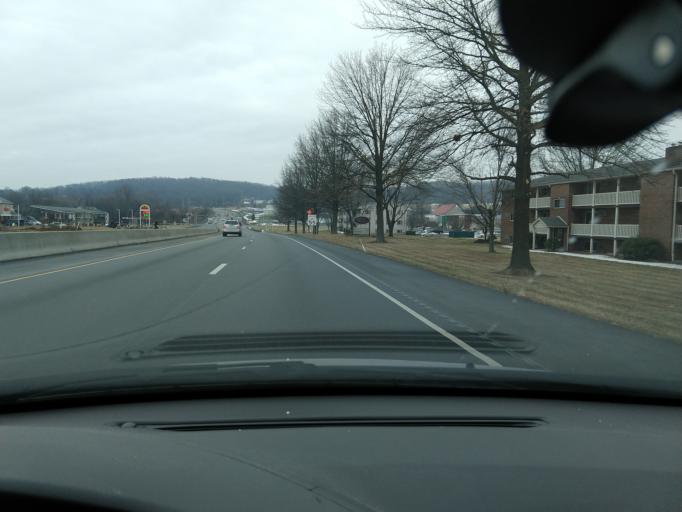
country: US
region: Pennsylvania
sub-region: Berks County
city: Boyertown
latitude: 40.3128
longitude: -75.6333
